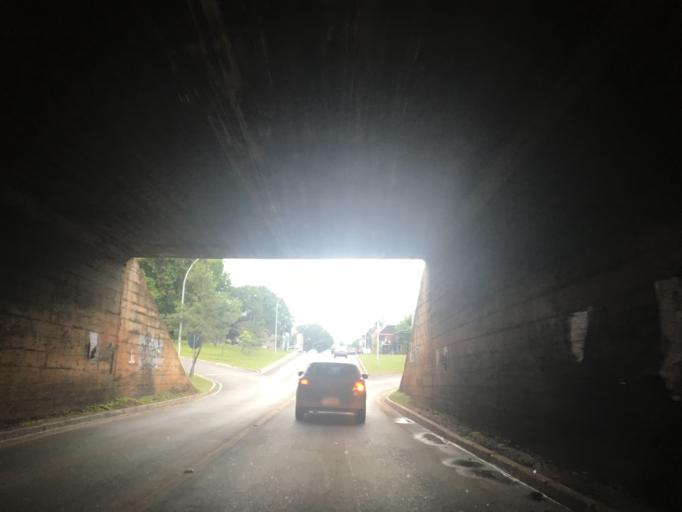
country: BR
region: Federal District
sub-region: Brasilia
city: Brasilia
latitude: -15.7397
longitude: -47.8919
